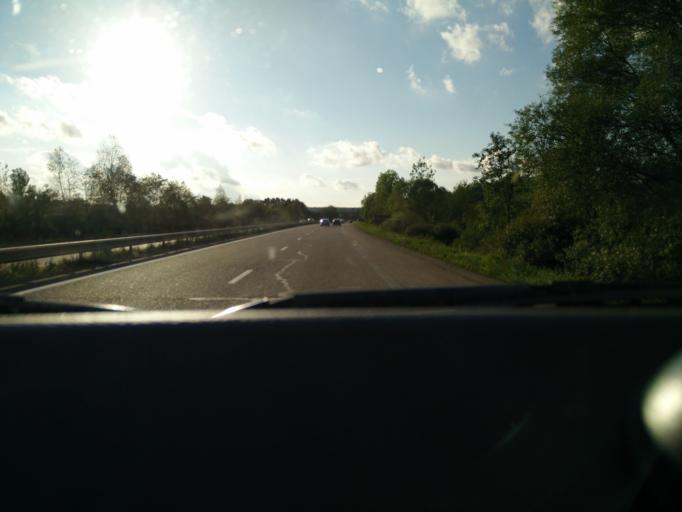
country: FR
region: Lorraine
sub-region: Departement de Meurthe-et-Moselle
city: Luneville
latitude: 48.5703
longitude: 6.5041
